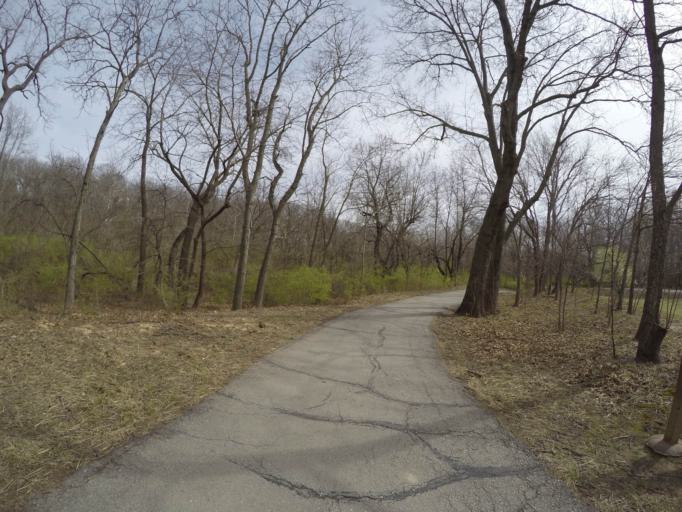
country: US
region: Kansas
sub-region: Johnson County
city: Leawood
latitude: 38.9170
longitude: -94.6322
